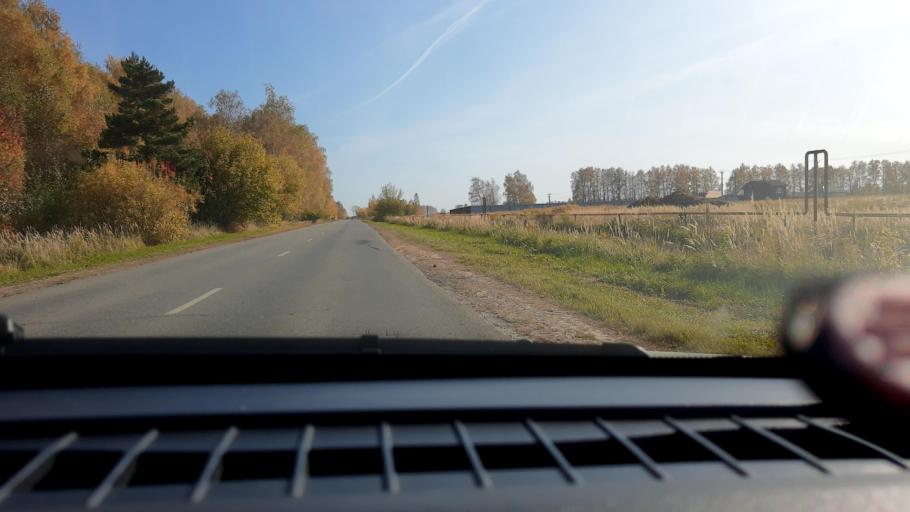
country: RU
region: Nizjnij Novgorod
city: Kstovo
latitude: 56.1542
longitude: 44.2780
